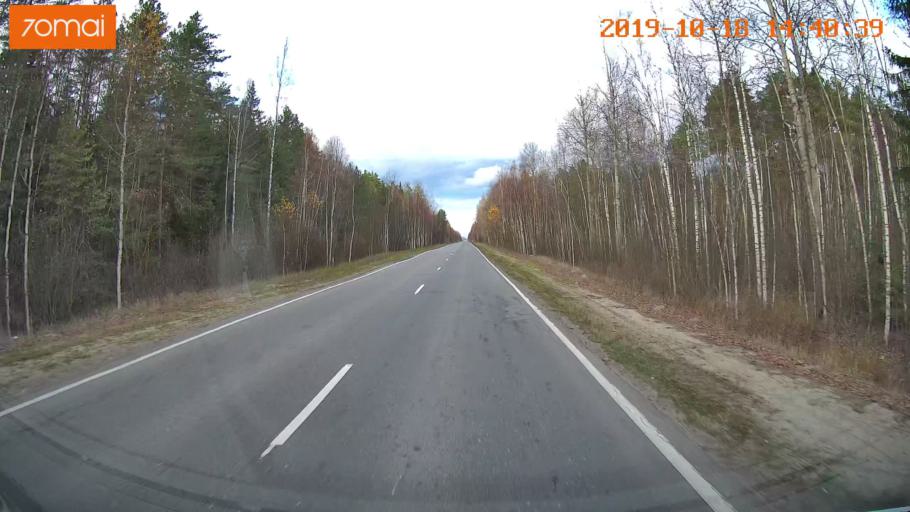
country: RU
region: Vladimir
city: Velikodvorskiy
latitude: 55.2800
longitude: 40.6694
